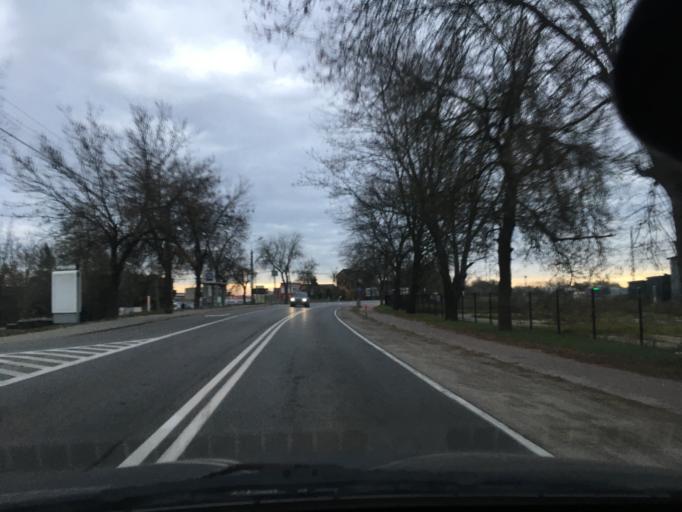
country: PL
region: Masovian Voivodeship
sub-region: Powiat piaseczynski
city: Lesznowola
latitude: 52.0961
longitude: 20.9226
